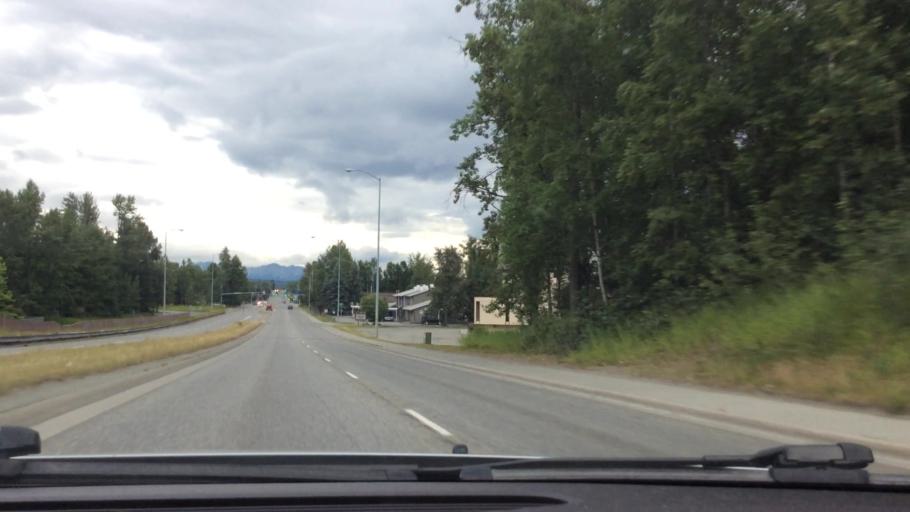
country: US
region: Alaska
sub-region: Anchorage Municipality
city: Anchorage
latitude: 61.2021
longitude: -149.7785
